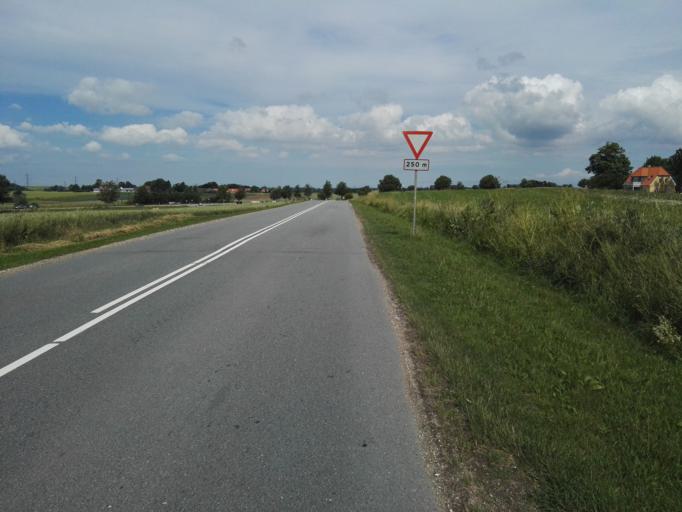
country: DK
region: Capital Region
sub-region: Frederikssund Kommune
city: Slangerup
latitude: 55.8632
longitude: 12.1788
